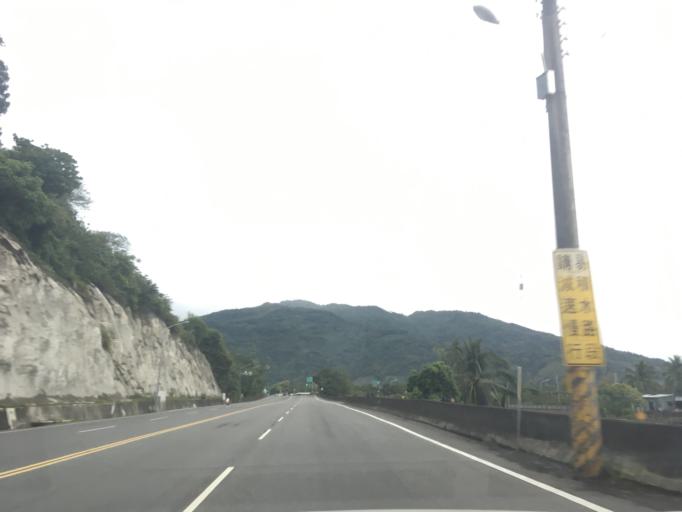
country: TW
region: Taiwan
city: Taitung City
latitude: 22.7536
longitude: 121.0536
